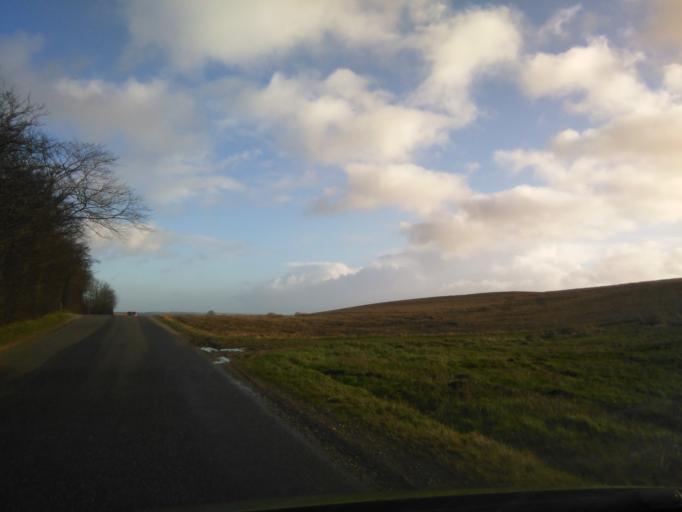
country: DK
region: Central Jutland
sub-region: Skanderborg Kommune
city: Skanderborg
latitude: 55.9876
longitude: 9.9050
